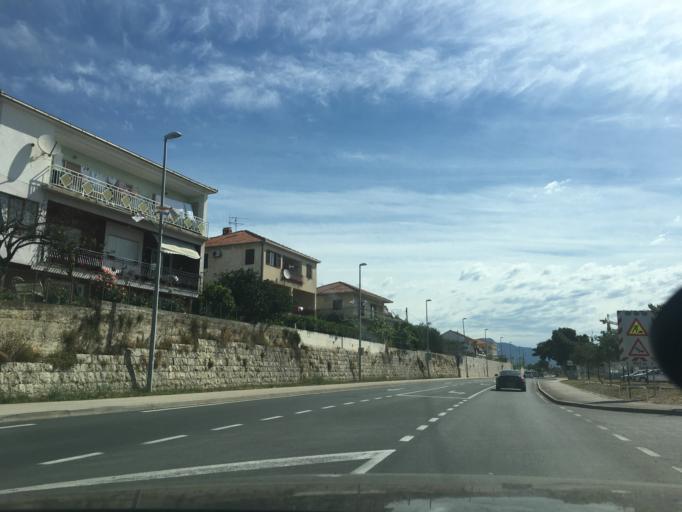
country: HR
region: Splitsko-Dalmatinska
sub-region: Grad Trogir
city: Trogir
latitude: 43.5201
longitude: 16.2577
